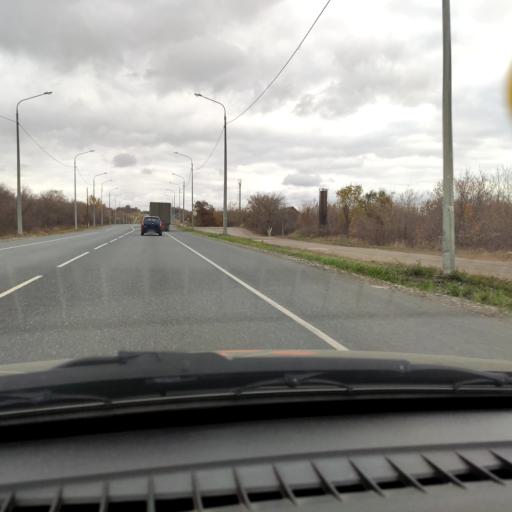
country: RU
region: Samara
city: Mezhdurechensk
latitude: 53.2501
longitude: 49.0251
